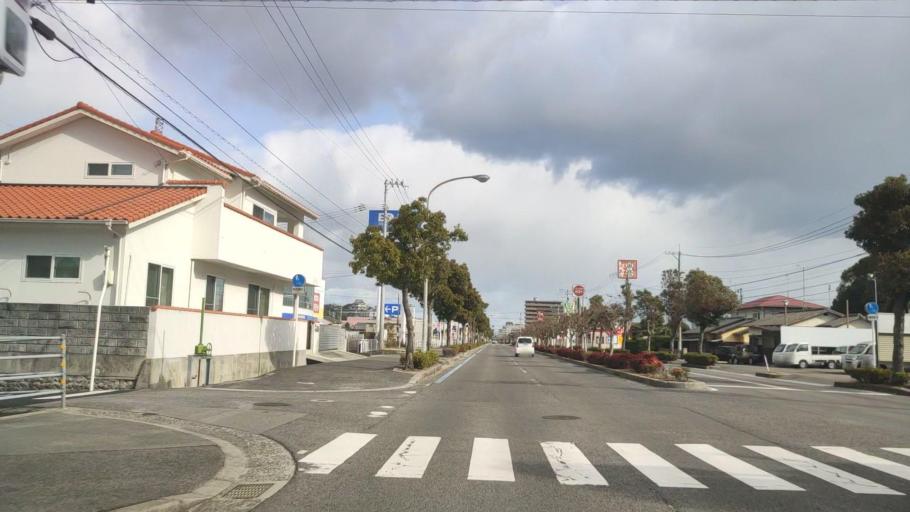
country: JP
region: Ehime
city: Hojo
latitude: 34.0583
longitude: 132.9814
